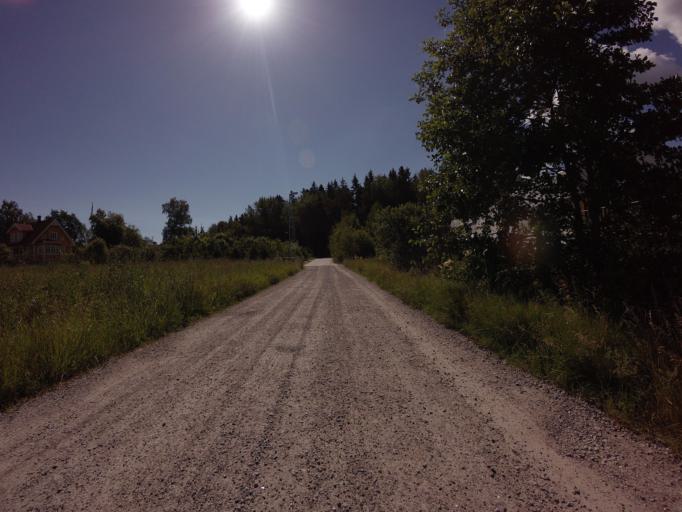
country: SE
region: Stockholm
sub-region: Jarfalla Kommun
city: Jakobsberg
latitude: 59.4637
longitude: 17.8816
